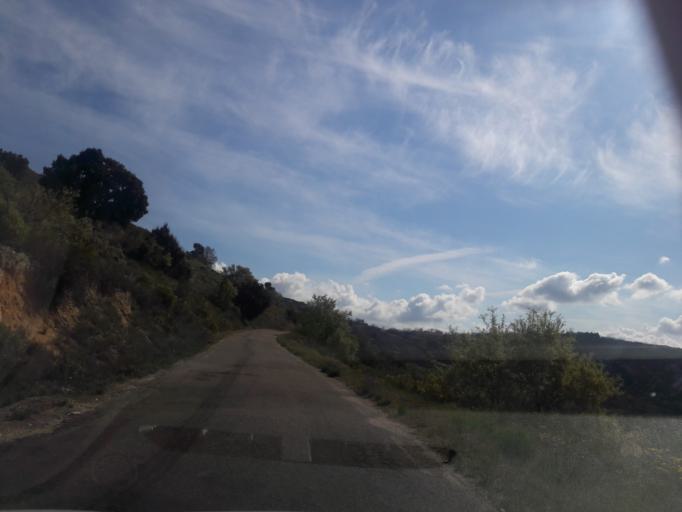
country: ES
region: Castille and Leon
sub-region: Provincia de Salamanca
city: San Esteban de la Sierra
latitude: 40.5066
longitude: -5.8856
